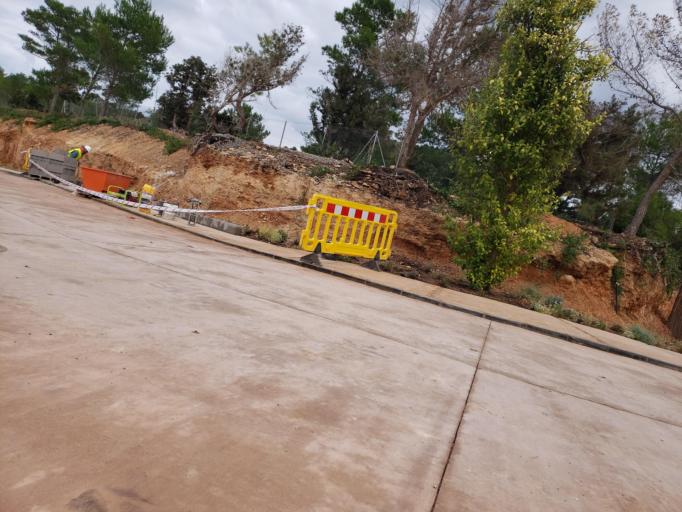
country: ES
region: Balearic Islands
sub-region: Illes Balears
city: Sant Joan de Labritja
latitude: 39.1101
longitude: 1.5090
